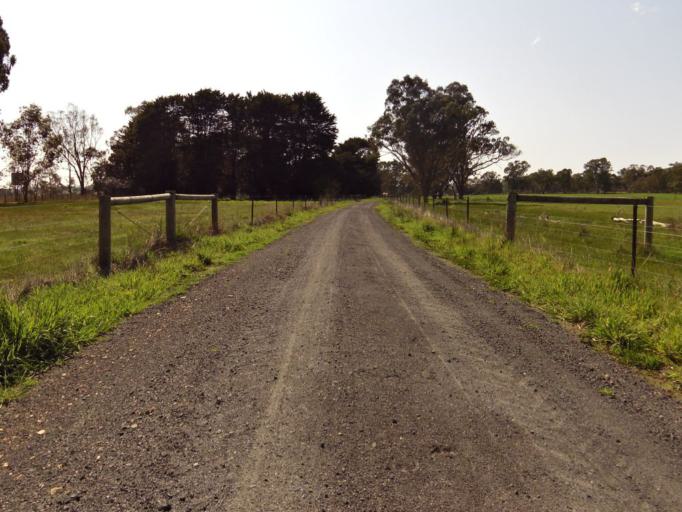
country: AU
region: Victoria
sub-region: Murrindindi
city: Alexandra
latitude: -37.1116
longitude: 145.6097
